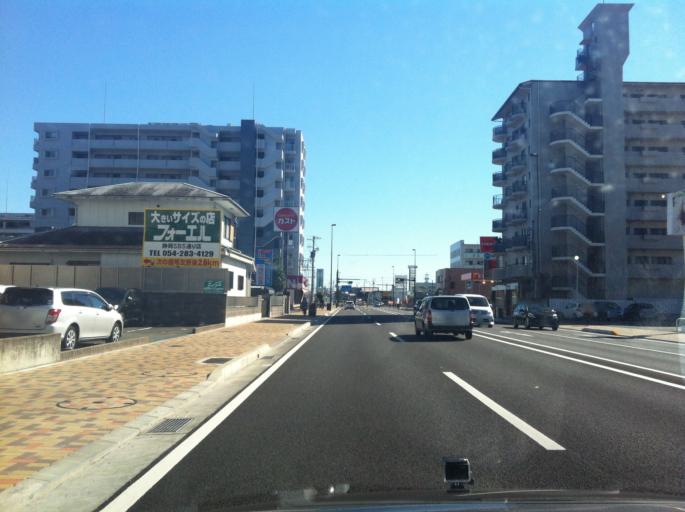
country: JP
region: Shizuoka
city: Shizuoka-shi
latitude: 34.9607
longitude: 138.3993
